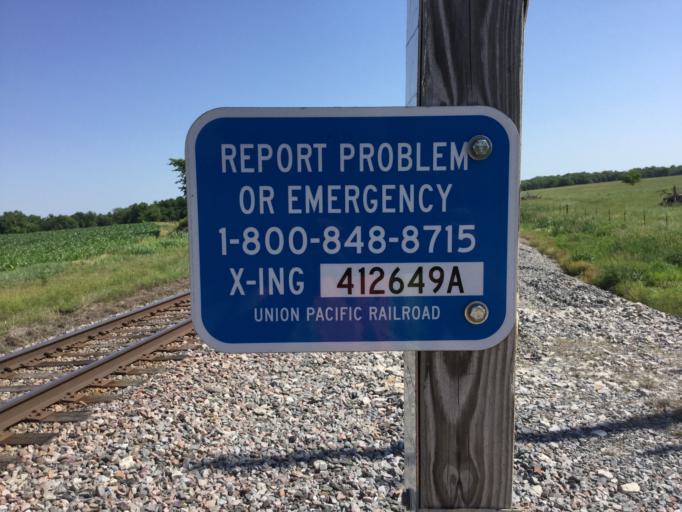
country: US
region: Kansas
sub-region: Anderson County
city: Garnett
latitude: 38.0669
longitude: -95.1602
